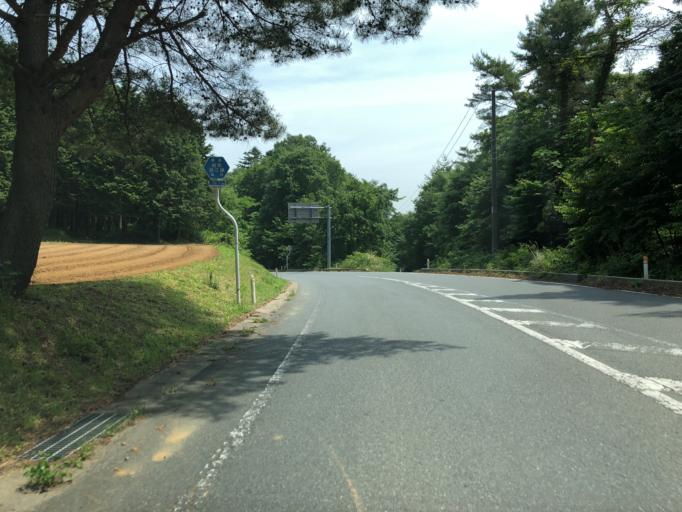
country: JP
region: Fukushima
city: Namie
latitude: 37.5902
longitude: 140.9345
